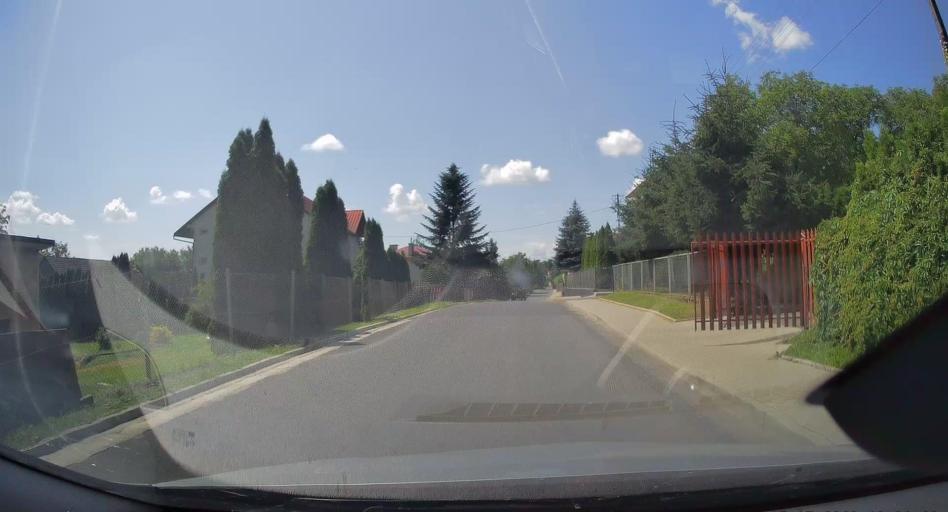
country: PL
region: Subcarpathian Voivodeship
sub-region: Powiat przemyski
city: Medyka
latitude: 49.8443
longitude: 22.8867
